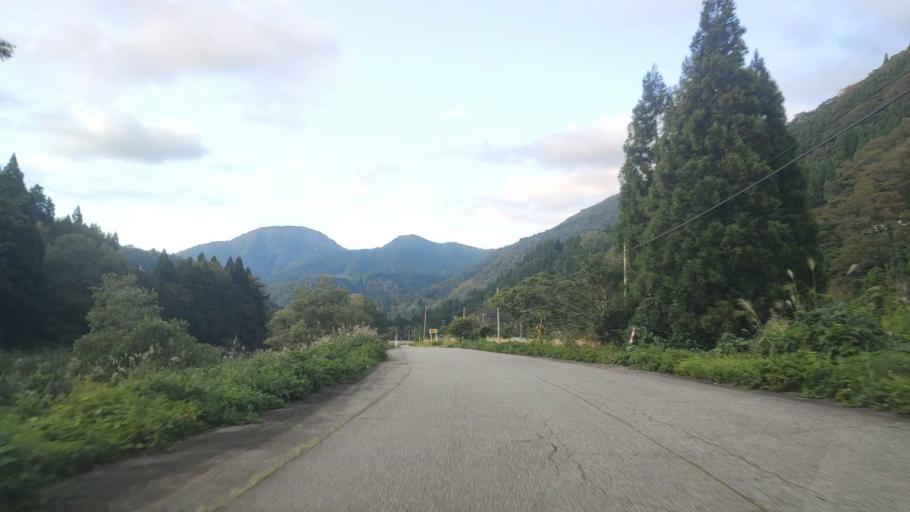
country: JP
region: Toyama
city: Yatsuomachi-higashikumisaka
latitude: 36.4660
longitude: 137.0860
